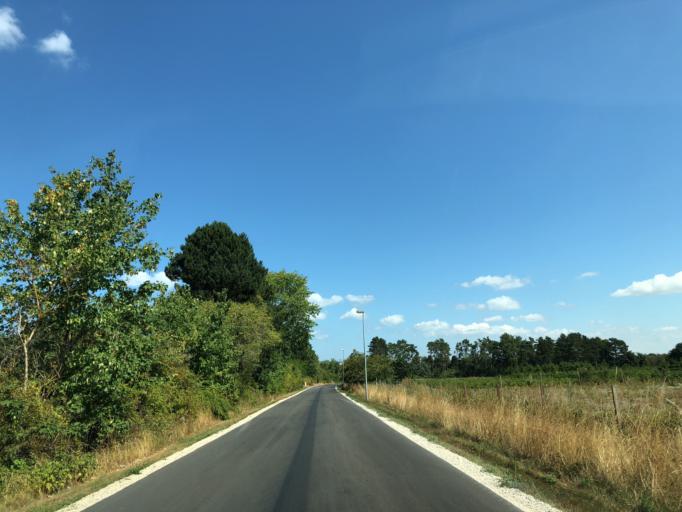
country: DK
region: Capital Region
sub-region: Halsnaes Kommune
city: Hundested
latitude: 55.9645
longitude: 11.9051
